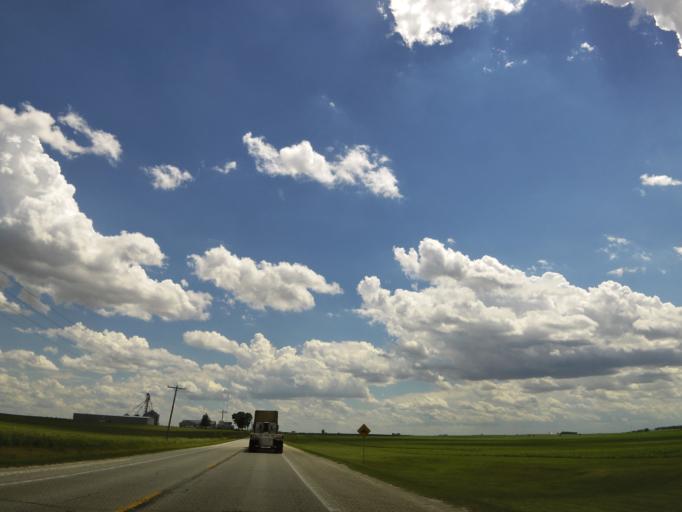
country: US
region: Iowa
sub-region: Benton County
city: Urbana
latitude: 42.3266
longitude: -91.8894
